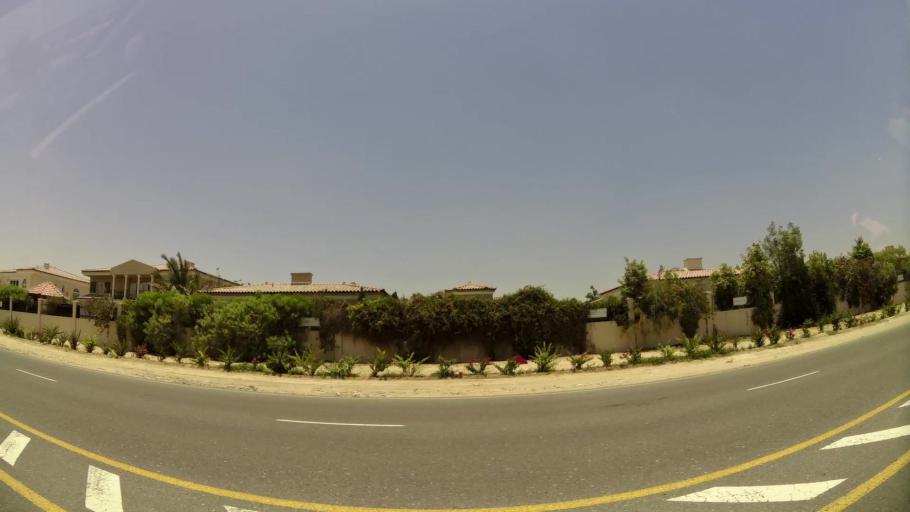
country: AE
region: Dubai
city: Dubai
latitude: 24.9913
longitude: 55.1667
